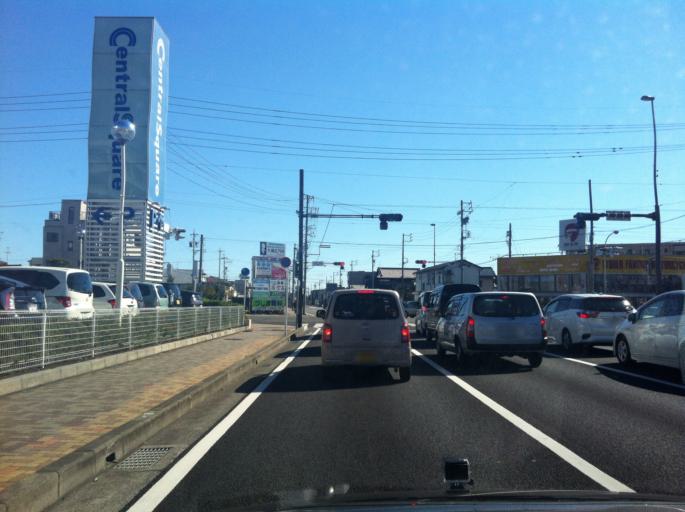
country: JP
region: Shizuoka
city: Shizuoka-shi
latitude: 34.9588
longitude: 138.4009
